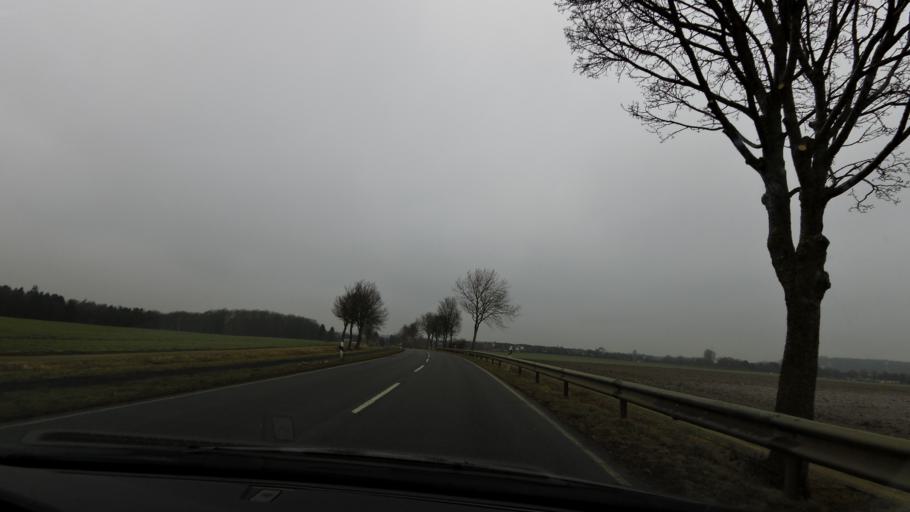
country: DE
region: North Rhine-Westphalia
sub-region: Regierungsbezirk Koln
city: Ubach-Palenberg
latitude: 50.9117
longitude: 6.1021
